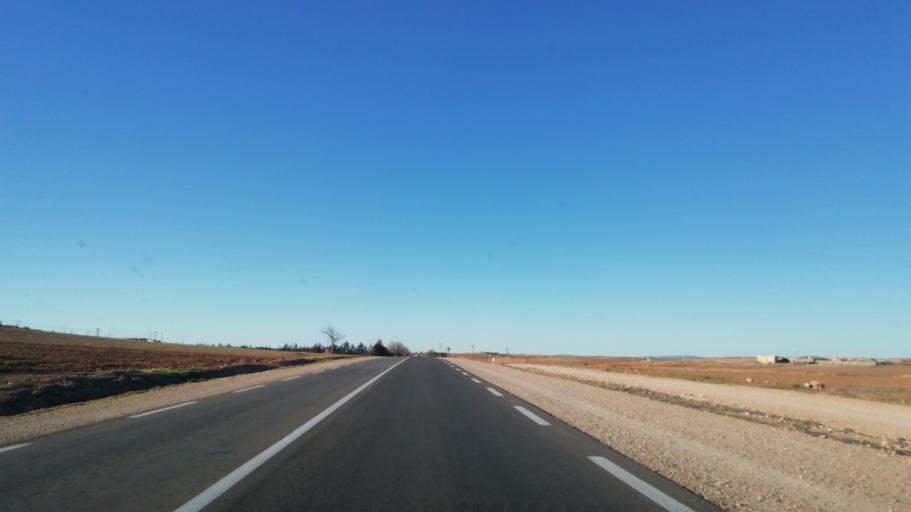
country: DZ
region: Tlemcen
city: Sebdou
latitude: 34.5159
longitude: -1.2861
